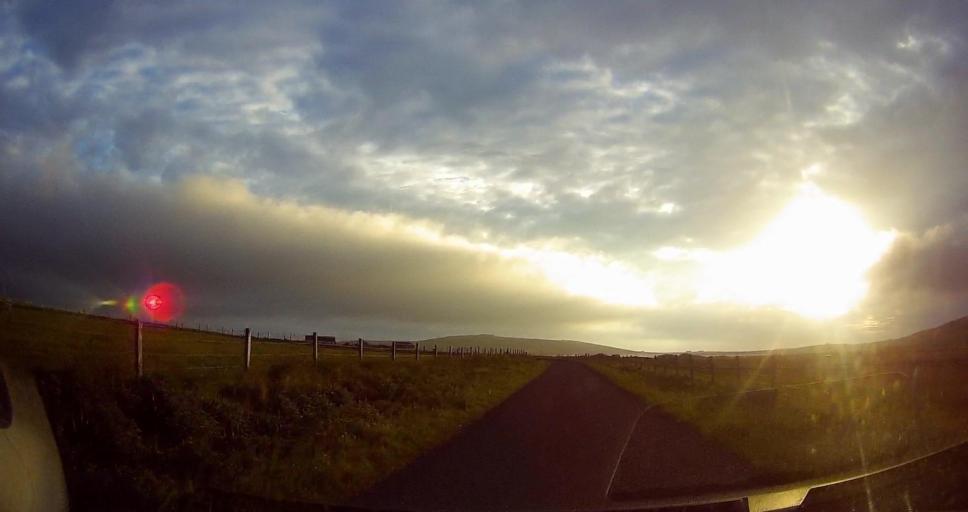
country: GB
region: Scotland
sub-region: Orkney Islands
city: Stromness
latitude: 59.1071
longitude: -3.2387
